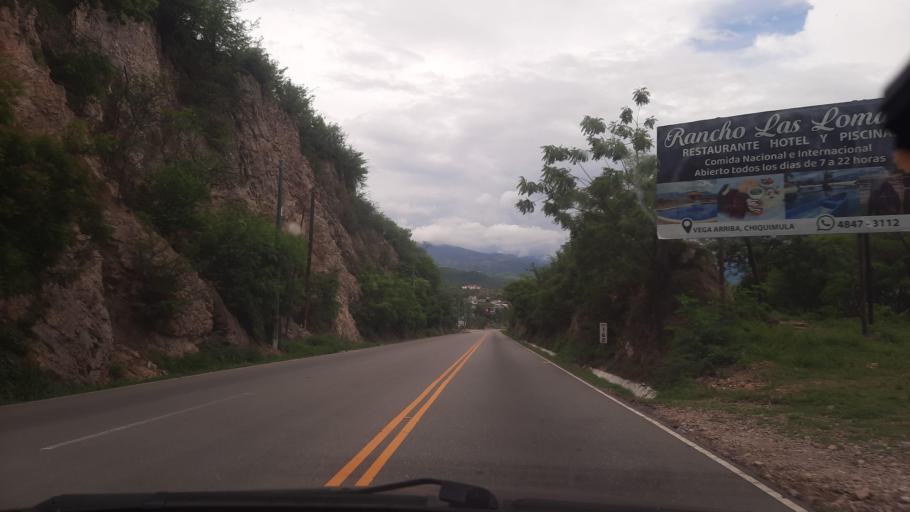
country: GT
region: Chiquimula
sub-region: Municipio de Chiquimula
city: Chiquimula
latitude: 14.8522
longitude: -89.5183
